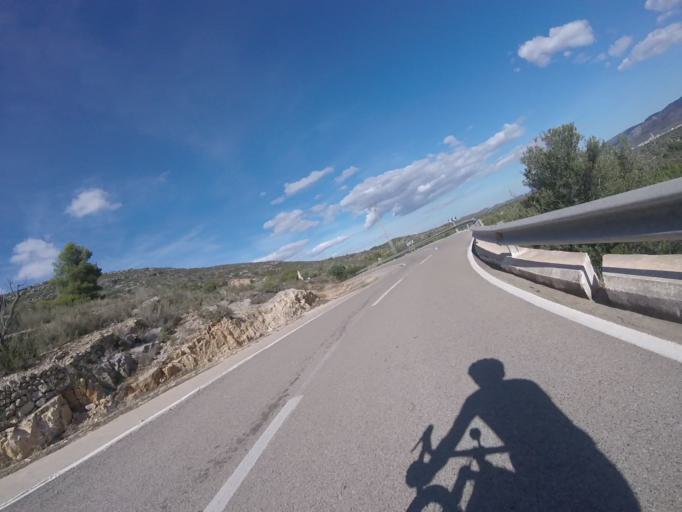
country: ES
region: Valencia
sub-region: Provincia de Castello
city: Alcala de Xivert
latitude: 40.2971
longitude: 0.1866
